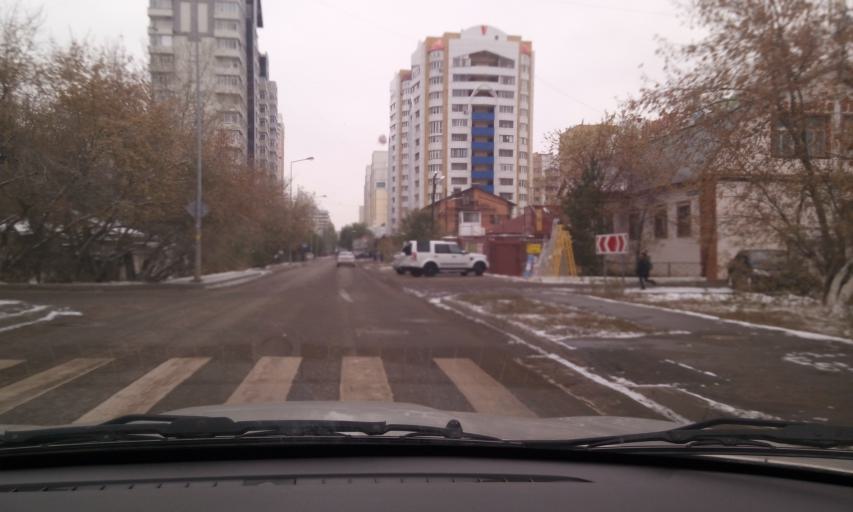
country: KZ
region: Astana Qalasy
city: Astana
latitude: 51.1600
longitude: 71.4329
